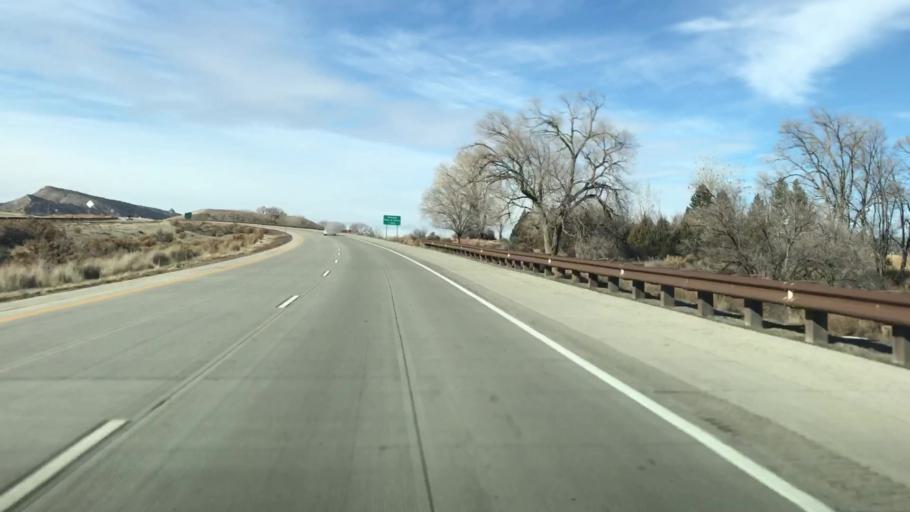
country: US
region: Colorado
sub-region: Mesa County
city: Loma
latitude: 39.1766
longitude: -108.8020
